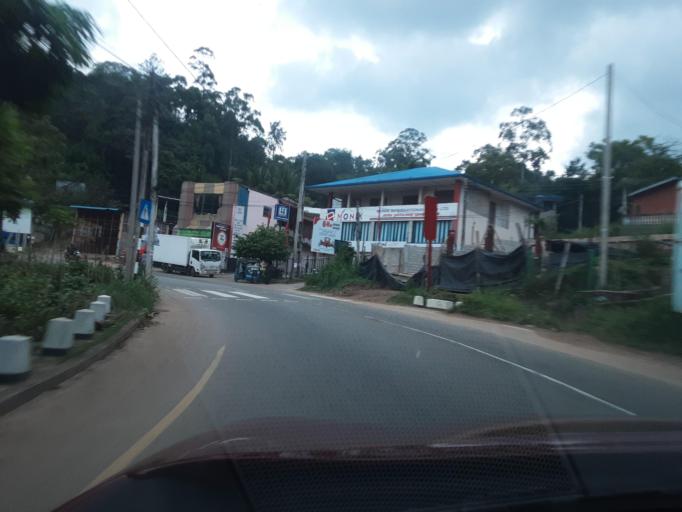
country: LK
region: Central
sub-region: Nuwara Eliya District
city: Nuwara Eliya
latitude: 6.9045
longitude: 80.9076
